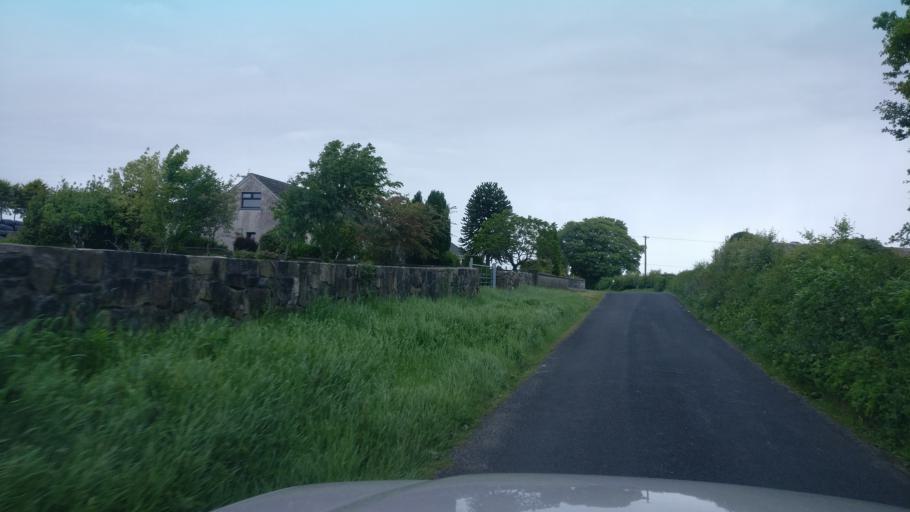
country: IE
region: Connaught
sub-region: County Galway
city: Loughrea
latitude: 53.1180
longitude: -8.4337
